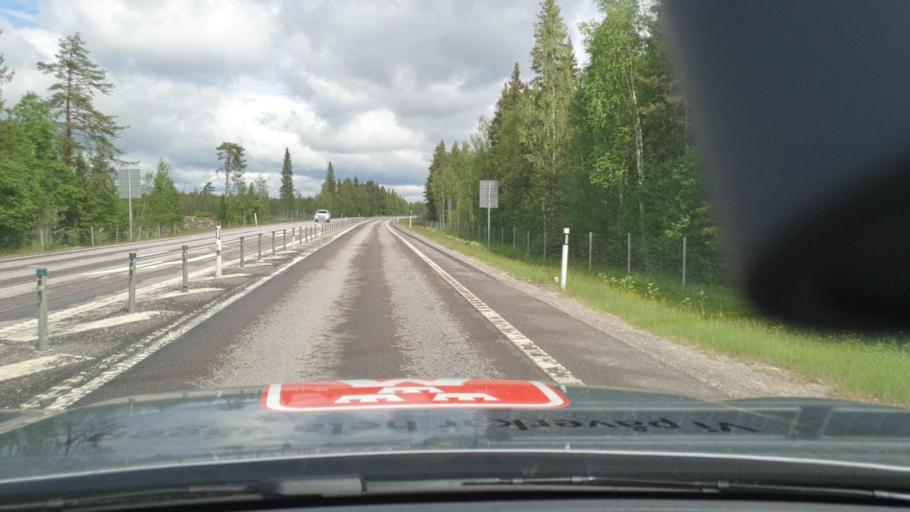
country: SE
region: Norrbotten
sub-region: Lulea Kommun
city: Ranea
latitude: 65.7945
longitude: 22.1825
